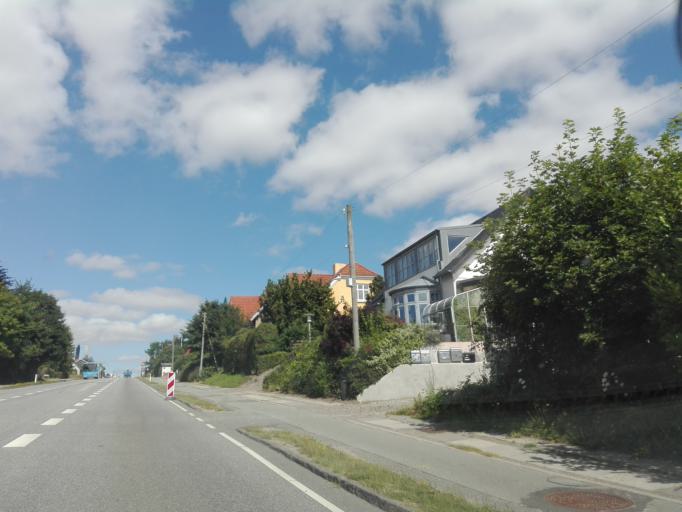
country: DK
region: Central Jutland
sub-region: Arhus Kommune
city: Trige
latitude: 56.2192
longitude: 10.1664
